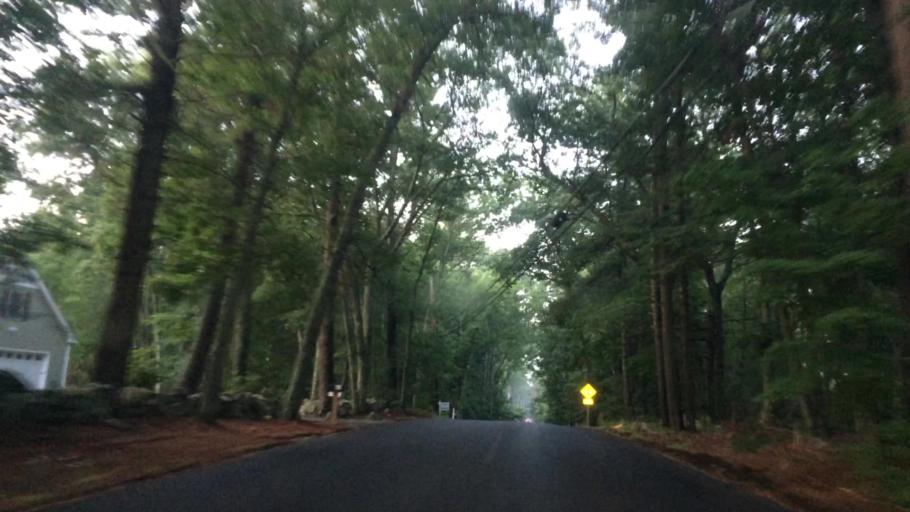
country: US
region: Massachusetts
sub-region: Middlesex County
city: North Reading
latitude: 42.6198
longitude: -71.0939
